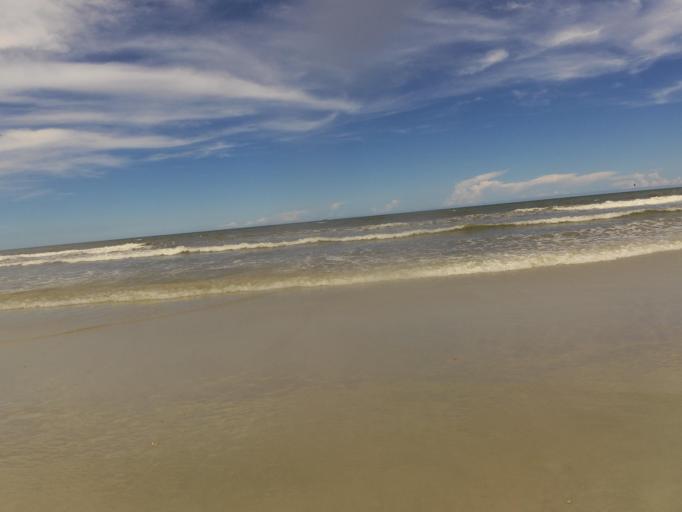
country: US
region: Florida
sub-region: Saint Johns County
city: Saint Augustine Beach
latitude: 29.8271
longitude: -81.2626
